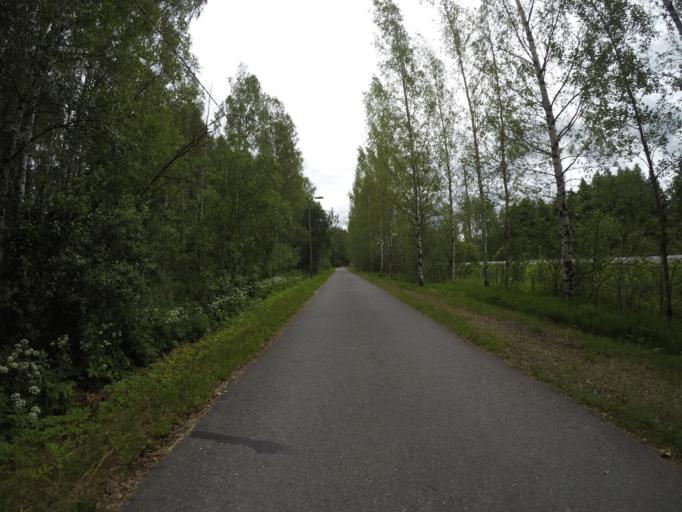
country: FI
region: Haeme
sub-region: Haemeenlinna
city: Haemeenlinna
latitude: 60.9902
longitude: 24.5010
